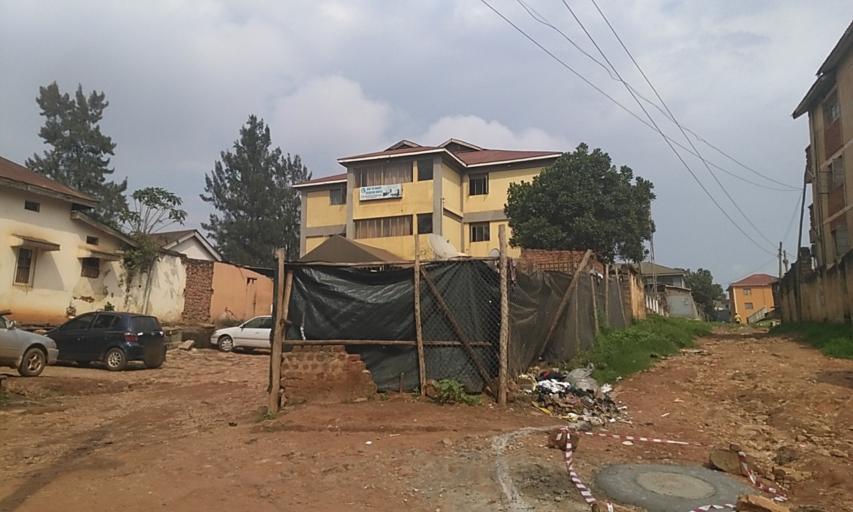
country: UG
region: Central Region
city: Kampala Central Division
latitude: 0.3121
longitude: 32.5662
